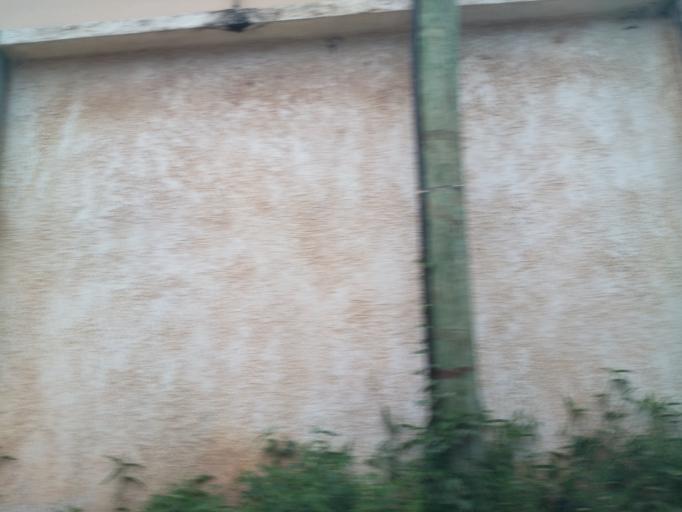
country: TZ
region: Dar es Salaam
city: Magomeni
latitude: -6.7726
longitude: 39.2758
